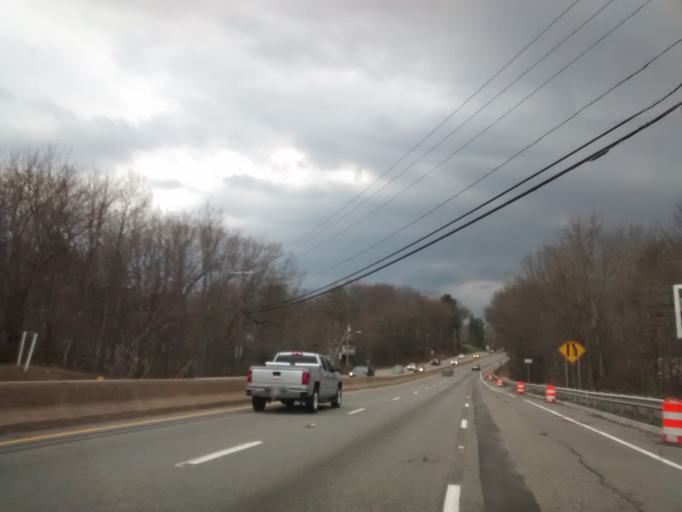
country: US
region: Massachusetts
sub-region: Worcester County
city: Sutton
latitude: 42.1643
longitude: -71.7431
